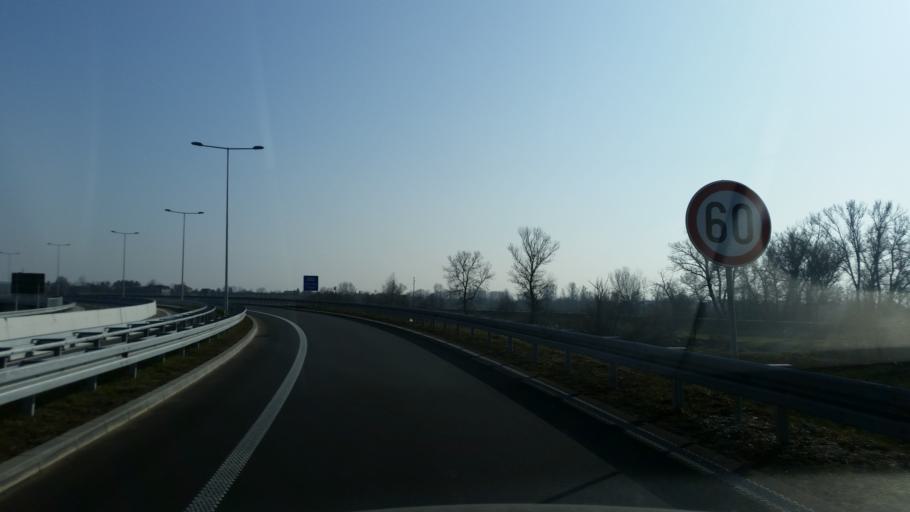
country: RS
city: Prislonica
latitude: 43.9180
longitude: 20.3958
